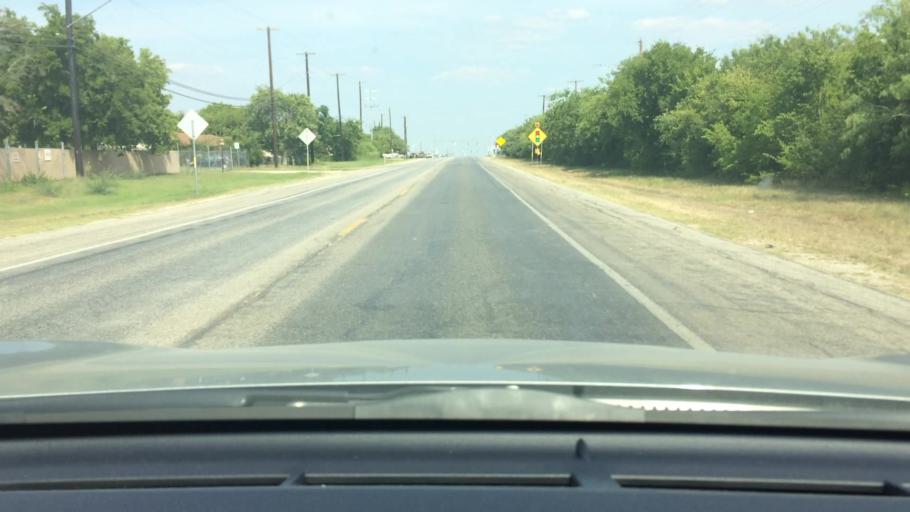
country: US
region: Texas
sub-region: Bexar County
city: China Grove
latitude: 29.3261
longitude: -98.4315
